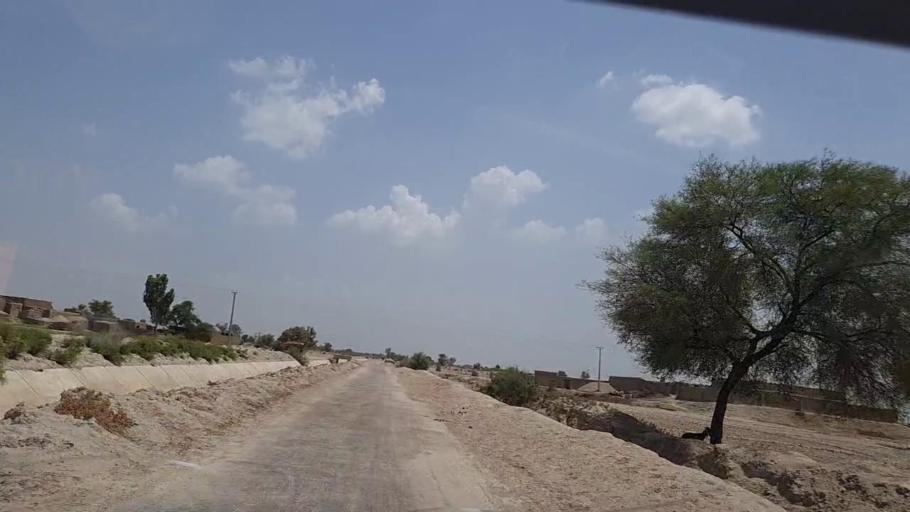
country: PK
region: Sindh
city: Bhan
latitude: 26.5296
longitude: 67.6332
